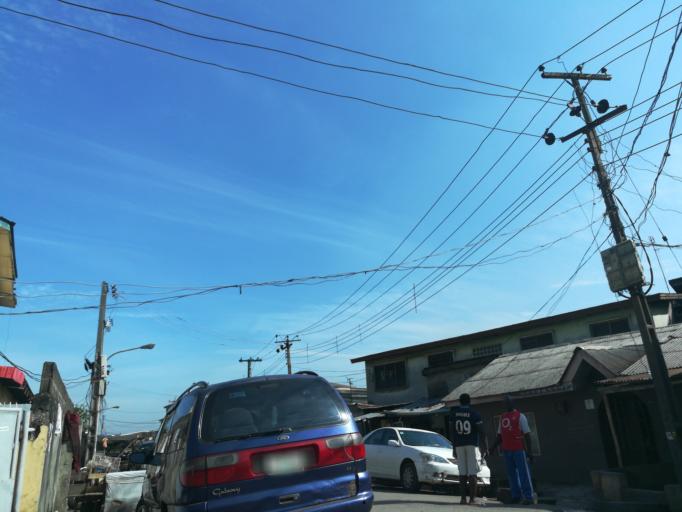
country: NG
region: Lagos
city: Ikeja
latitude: 6.5987
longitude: 3.3414
